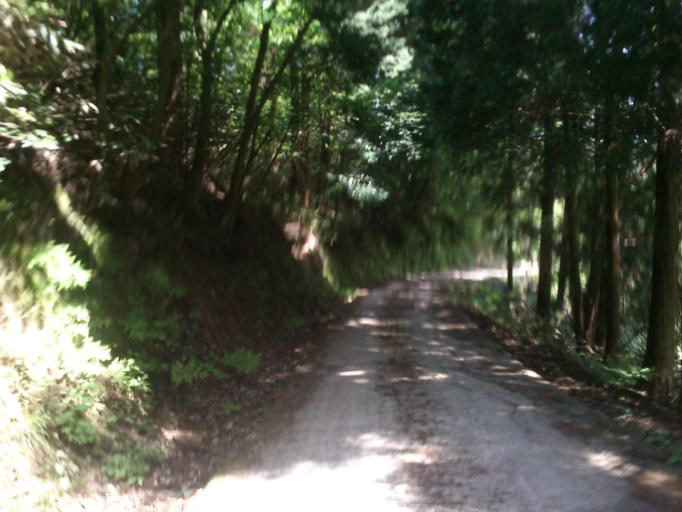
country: JP
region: Kyoto
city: Miyazu
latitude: 35.6096
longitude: 135.1954
